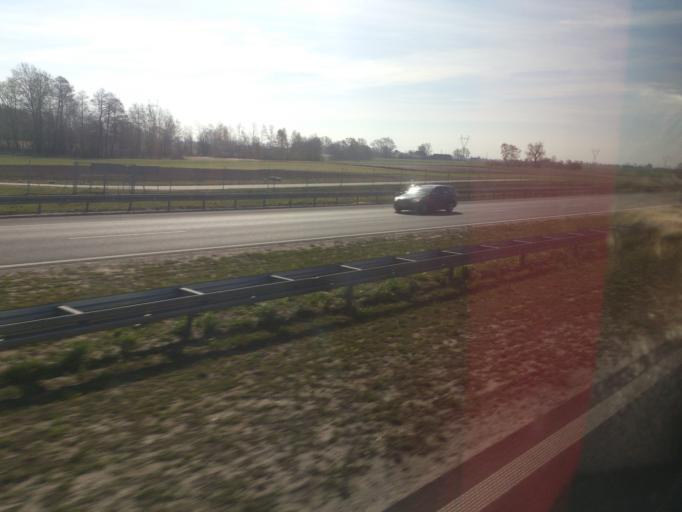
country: PL
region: Kujawsko-Pomorskie
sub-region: Powiat aleksandrowski
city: Waganiec
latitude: 52.7738
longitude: 18.8459
